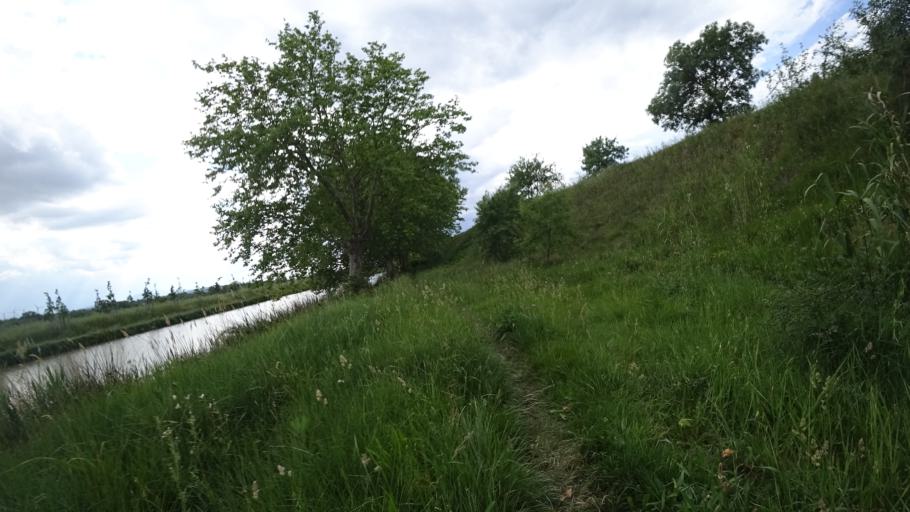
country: FR
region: Languedoc-Roussillon
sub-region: Departement de l'Aude
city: Canet
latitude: 43.2484
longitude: 2.8486
